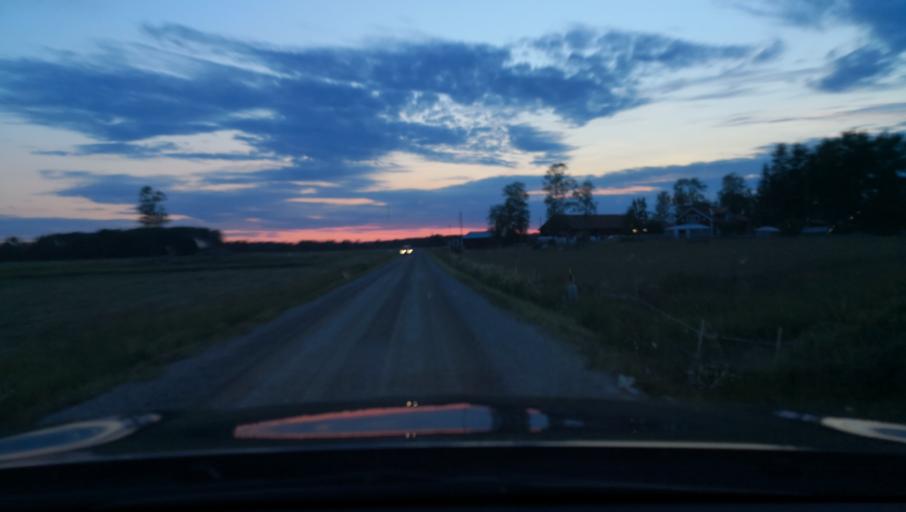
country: SE
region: Uppsala
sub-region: Osthammars Kommun
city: Bjorklinge
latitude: 60.0071
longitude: 17.3319
